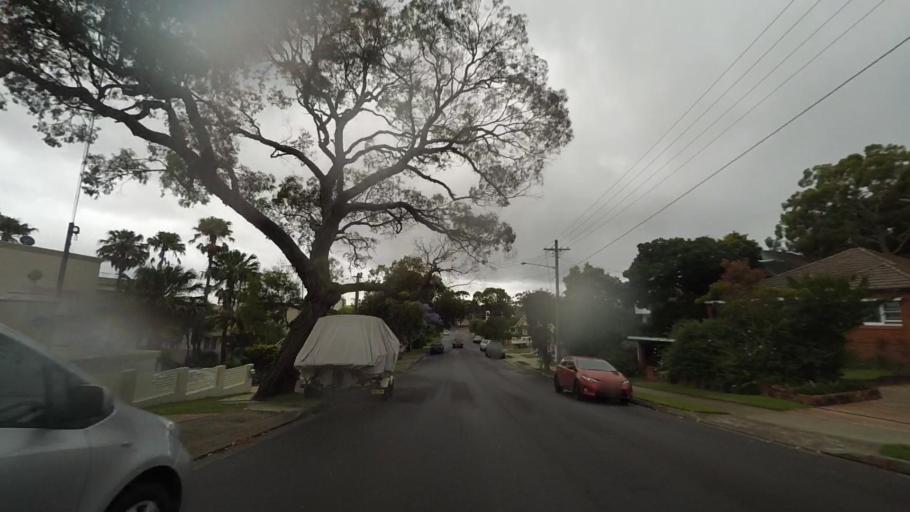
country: AU
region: New South Wales
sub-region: Kogarah
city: Kogarah
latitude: -33.9956
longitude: 151.1255
